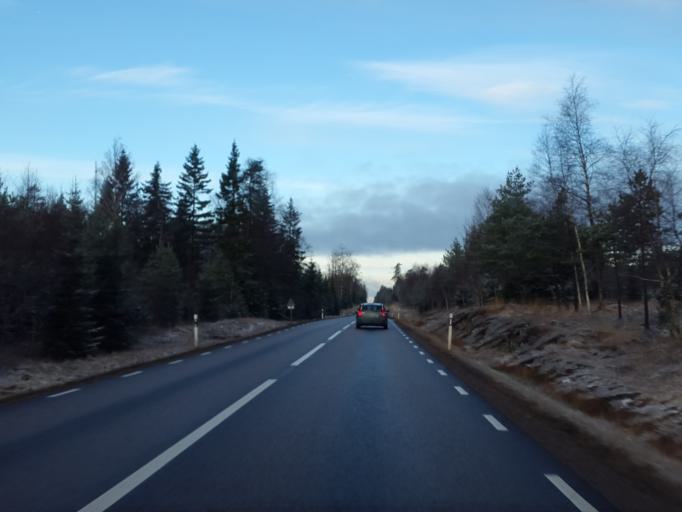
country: SE
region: Vaestra Goetaland
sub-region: Boras Kommun
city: Sjomarken
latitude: 57.7546
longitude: 12.8602
